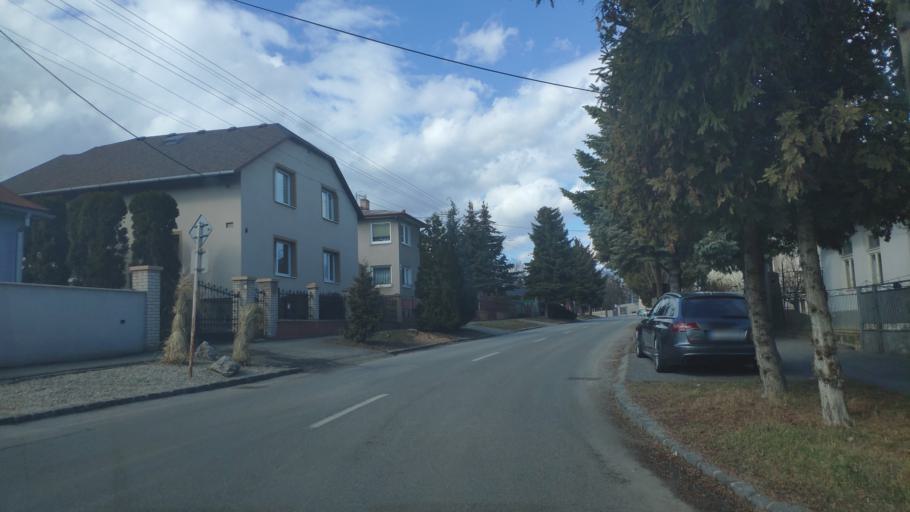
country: SK
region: Kosicky
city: Kosice
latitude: 48.6747
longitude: 21.2658
